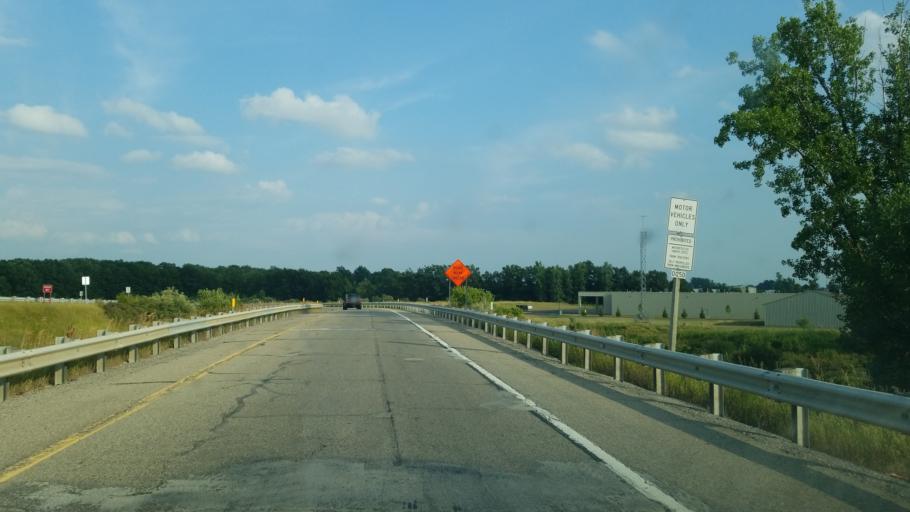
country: US
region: Michigan
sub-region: Gratiot County
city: Alma
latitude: 43.4073
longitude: -84.6634
